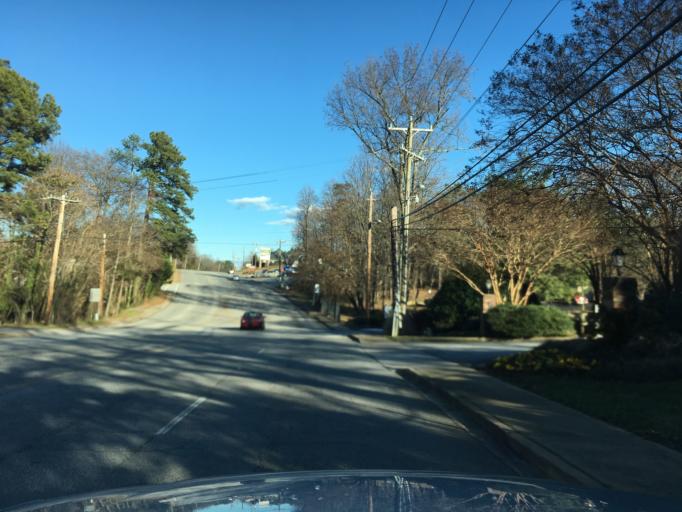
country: US
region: South Carolina
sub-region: Greenville County
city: Wade Hampton
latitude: 34.8695
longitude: -82.3513
